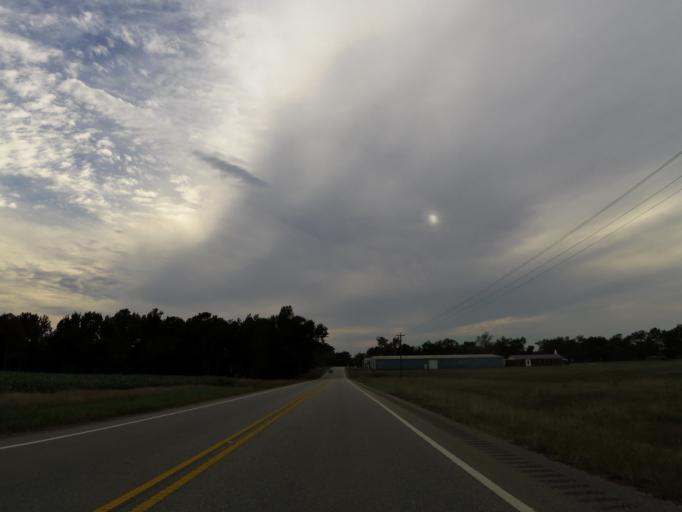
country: US
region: Alabama
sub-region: Monroe County
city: Frisco City
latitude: 31.3088
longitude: -87.4915
